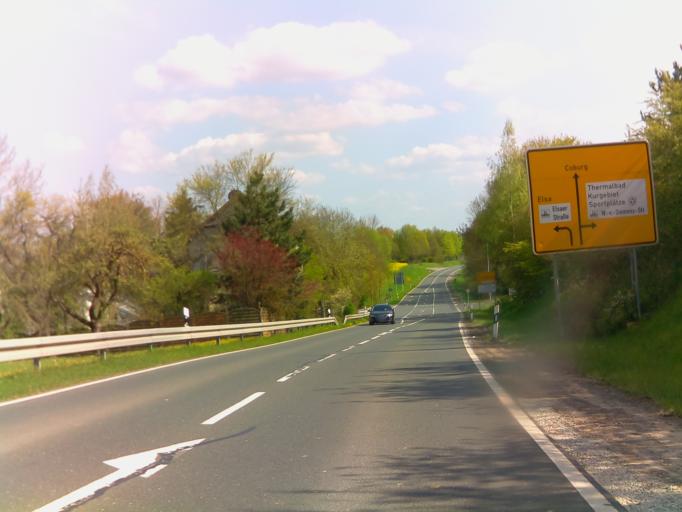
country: DE
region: Thuringia
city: Veilsdorf
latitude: 50.3385
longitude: 10.7901
